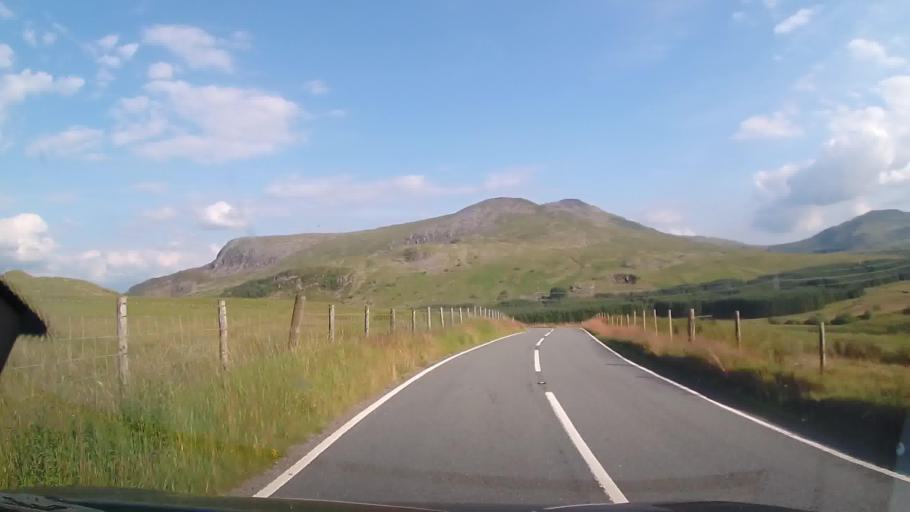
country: GB
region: Wales
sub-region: Conwy
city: Betws-y-Coed
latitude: 52.9412
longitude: -3.7690
